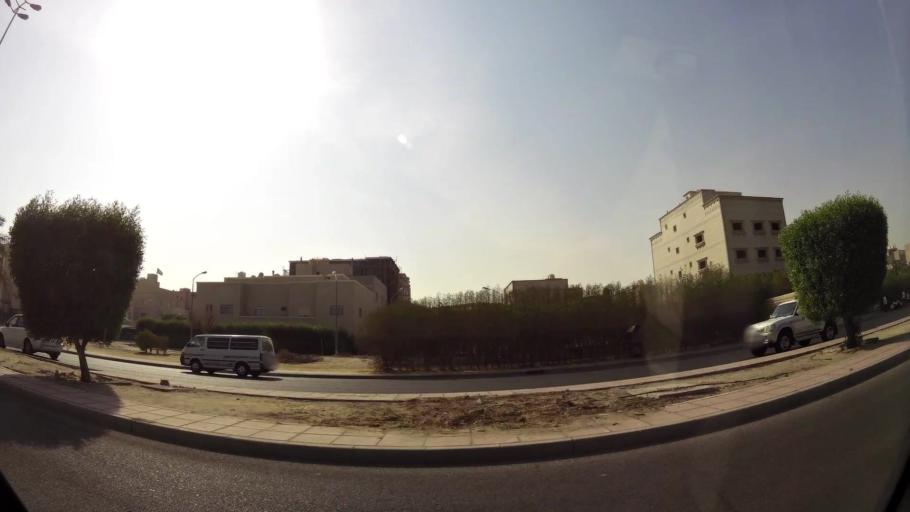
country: KW
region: Mubarak al Kabir
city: Mubarak al Kabir
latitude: 29.1717
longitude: 48.0852
